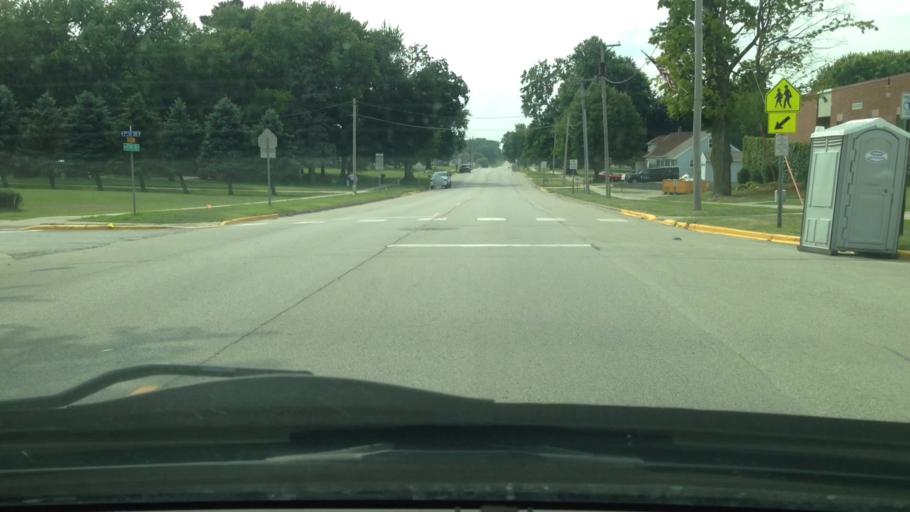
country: US
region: Minnesota
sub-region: Wabasha County
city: Plainview
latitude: 44.1650
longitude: -92.1750
